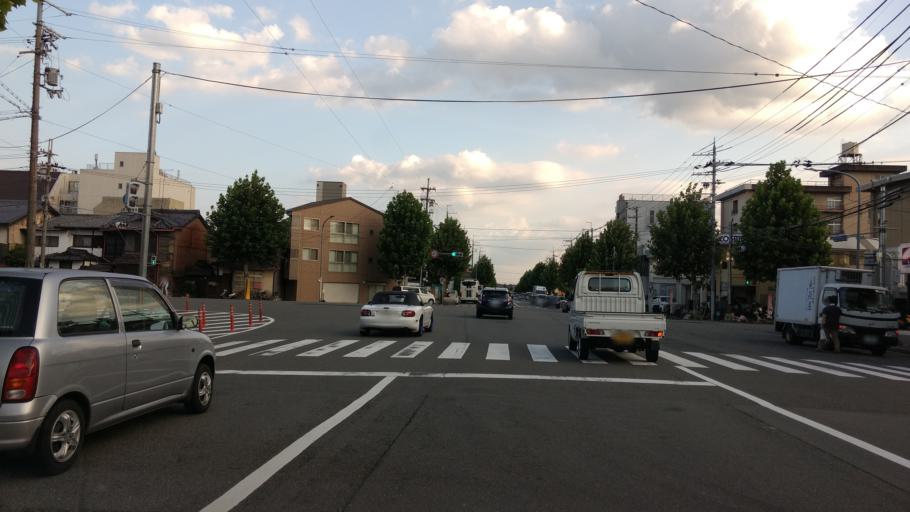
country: JP
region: Kyoto
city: Kyoto
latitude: 34.9932
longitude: 135.7393
